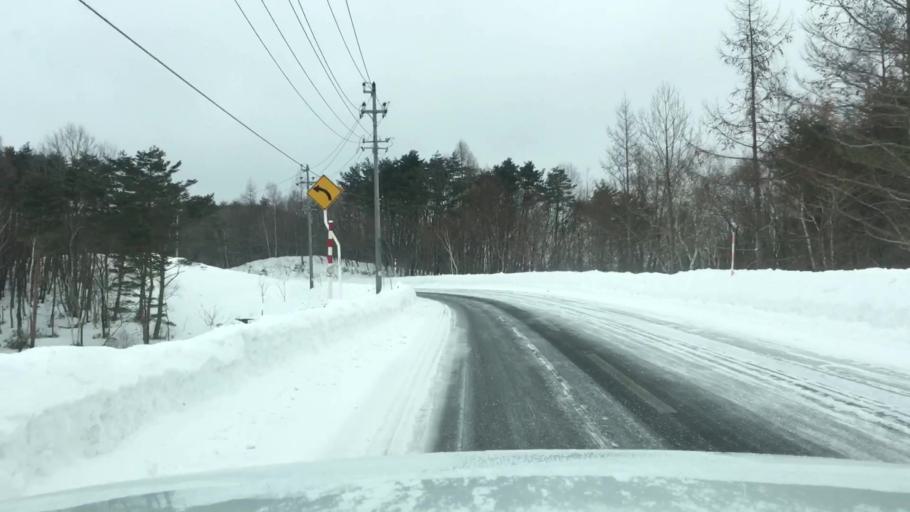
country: JP
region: Iwate
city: Shizukuishi
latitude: 39.9720
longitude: 141.0026
